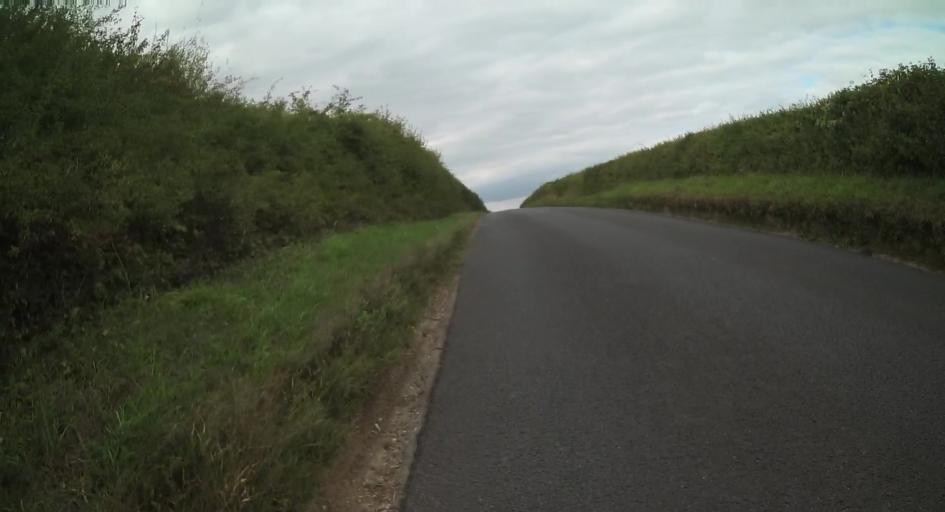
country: GB
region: England
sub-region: Isle of Wight
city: Yarmouth
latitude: 50.6958
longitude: -1.4827
